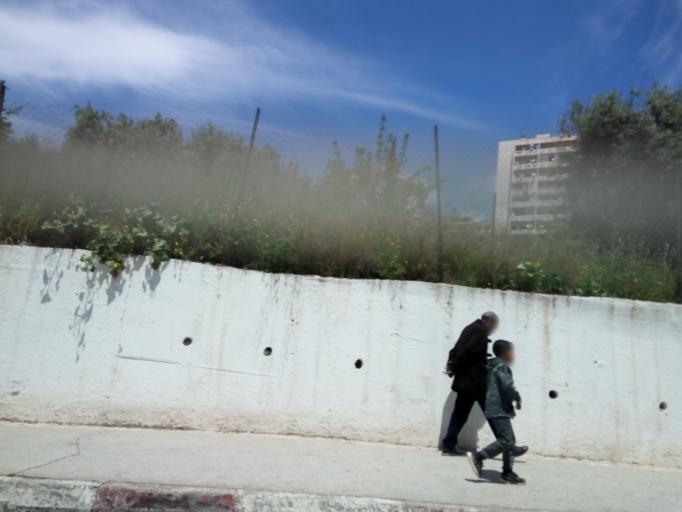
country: DZ
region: Constantine
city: Constantine
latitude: 36.3726
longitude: 6.6205
